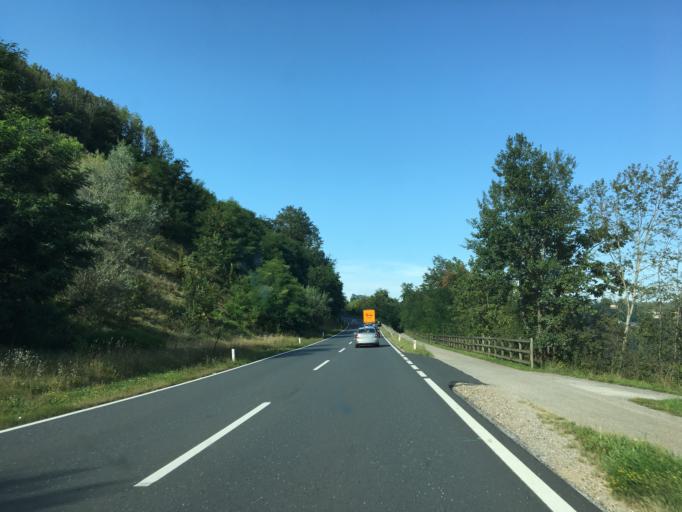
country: AT
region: Carinthia
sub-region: Politischer Bezirk Volkermarkt
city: Voelkermarkt
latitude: 46.6516
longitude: 14.6297
